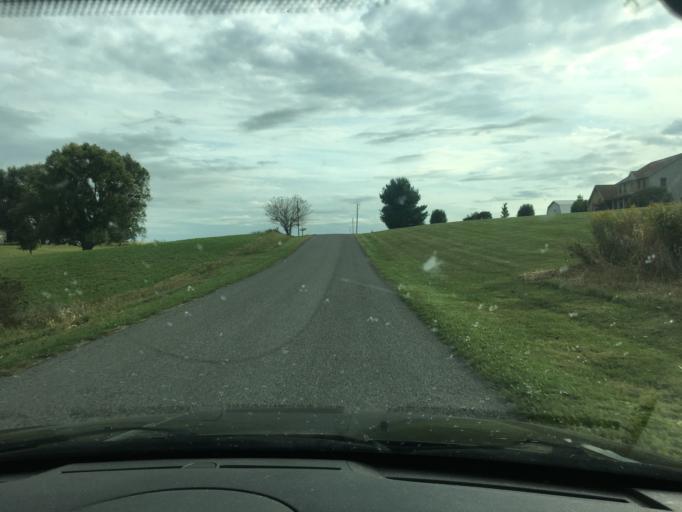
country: US
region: Ohio
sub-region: Logan County
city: Bellefontaine
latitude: 40.3234
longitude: -83.8060
